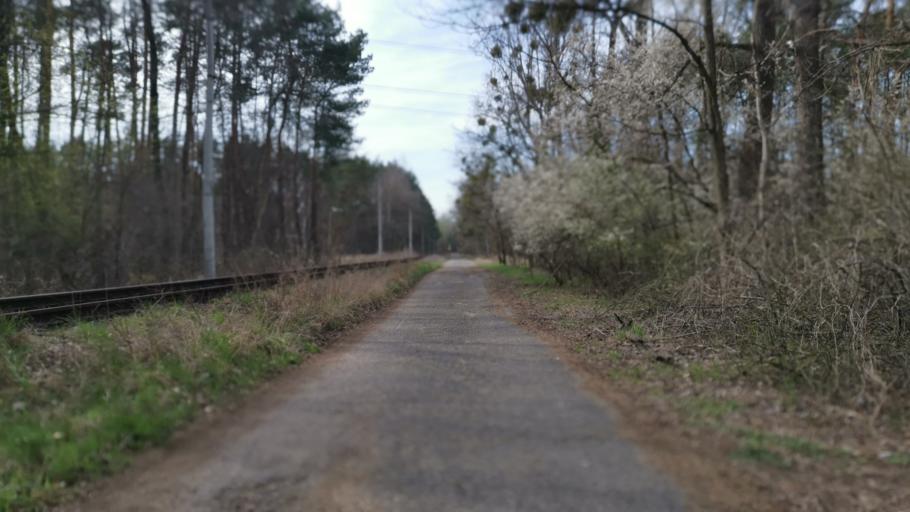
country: SK
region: Trnavsky
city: Gbely
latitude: 48.6658
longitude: 17.0591
